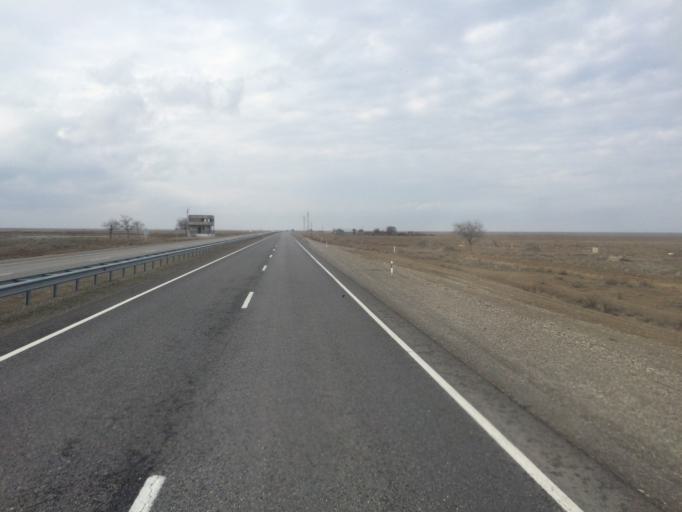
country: KZ
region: Ongtustik Qazaqstan
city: Turkestan
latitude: 43.5255
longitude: 67.7942
